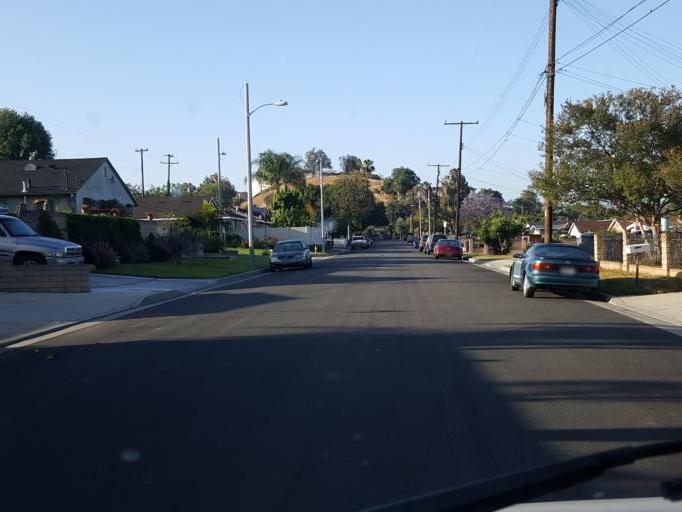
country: US
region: California
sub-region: Los Angeles County
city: Valinda
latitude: 34.0470
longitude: -117.9213
